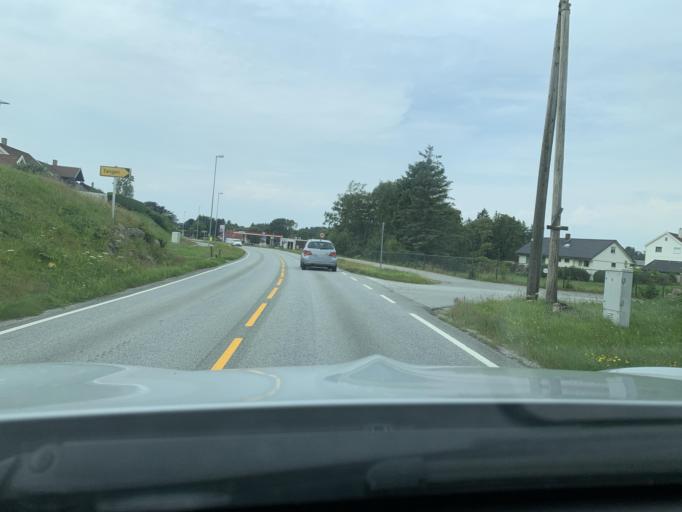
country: NO
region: Rogaland
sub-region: Time
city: Bryne
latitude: 58.7348
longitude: 5.6714
